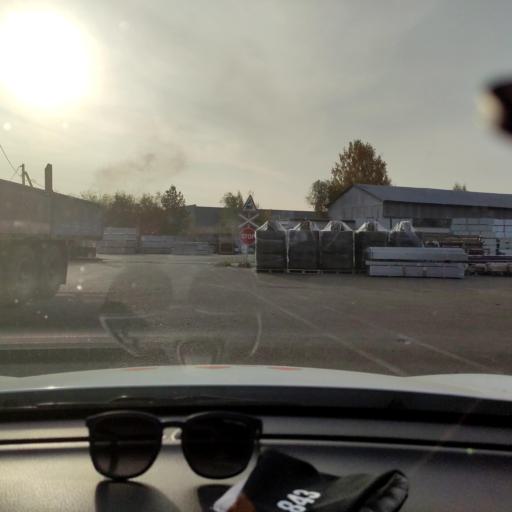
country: RU
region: Tatarstan
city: Staroye Arakchino
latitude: 55.8355
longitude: 49.0289
